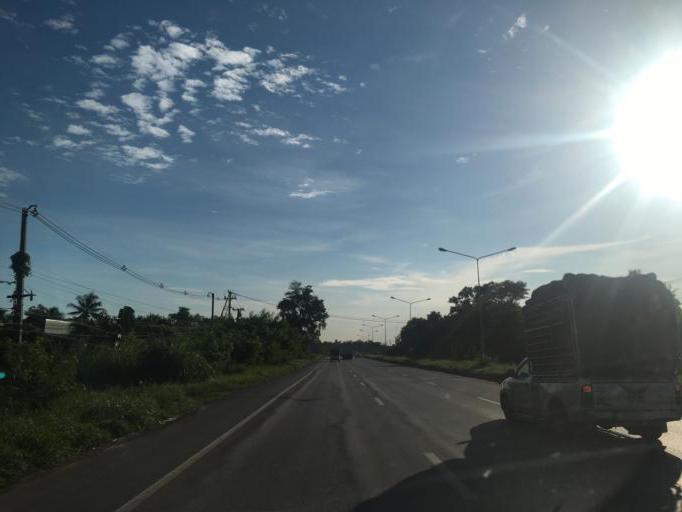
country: TH
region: Changwat Udon Thani
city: Kut Chap
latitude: 17.3342
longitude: 102.6585
